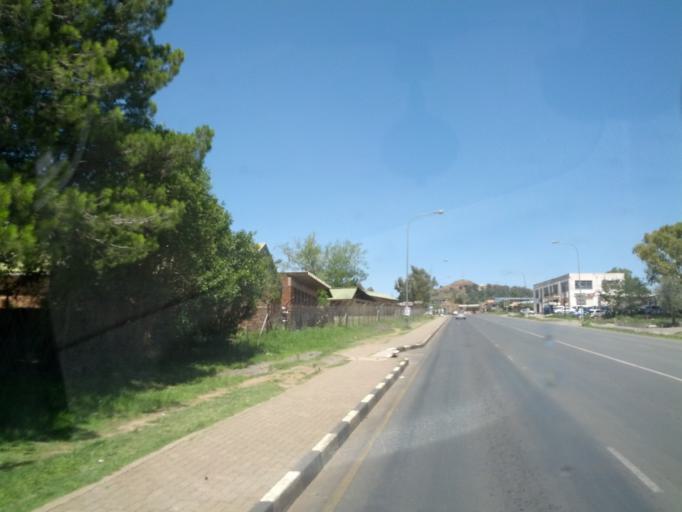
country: LS
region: Maseru
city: Maseru
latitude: -29.3044
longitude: 27.4834
